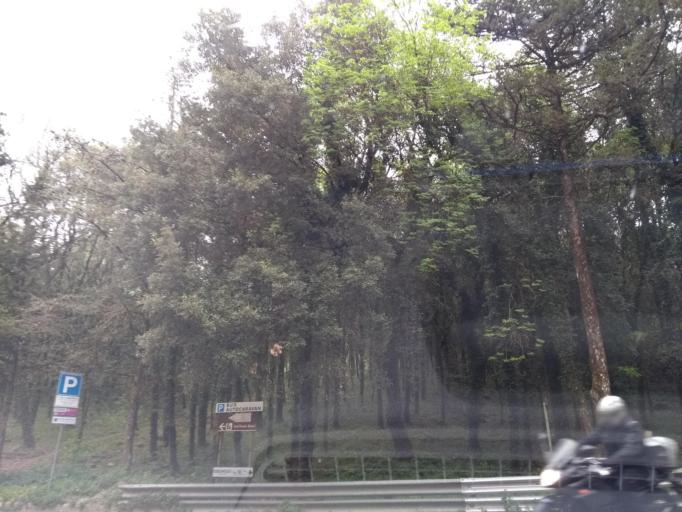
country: IT
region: Sicily
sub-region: Trapani
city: Erice
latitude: 38.0403
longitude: 12.5845
